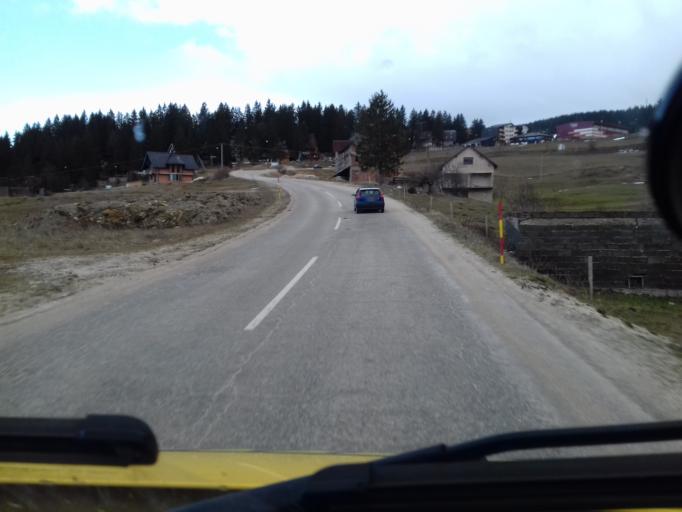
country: BA
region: Federation of Bosnia and Herzegovina
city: Turbe
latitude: 44.3142
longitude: 17.5645
